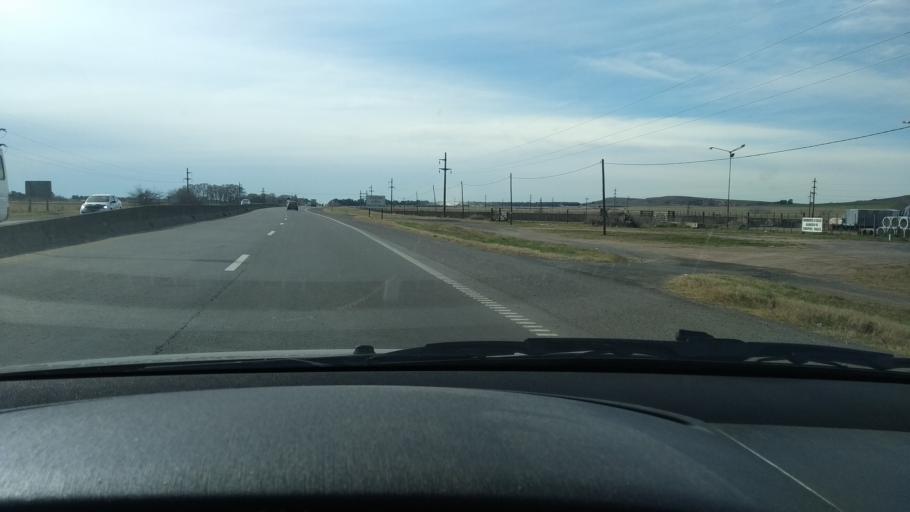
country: AR
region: Buenos Aires
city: Olavarria
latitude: -36.9353
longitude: -60.2281
